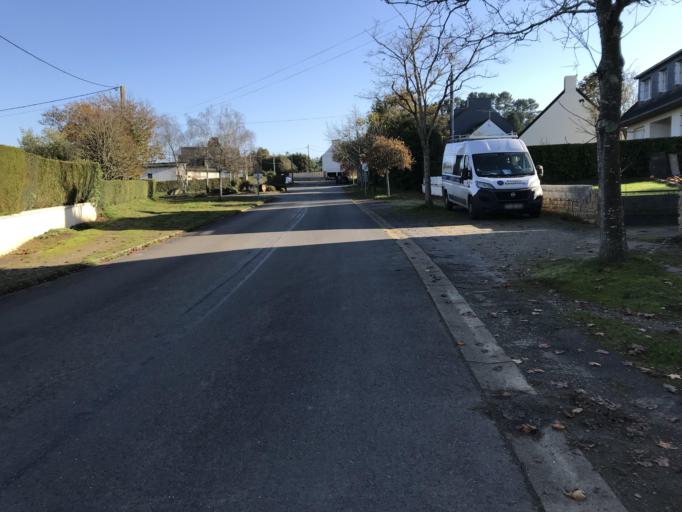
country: FR
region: Brittany
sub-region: Departement du Finistere
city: Hopital-Camfrout
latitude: 48.3247
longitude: -4.2369
